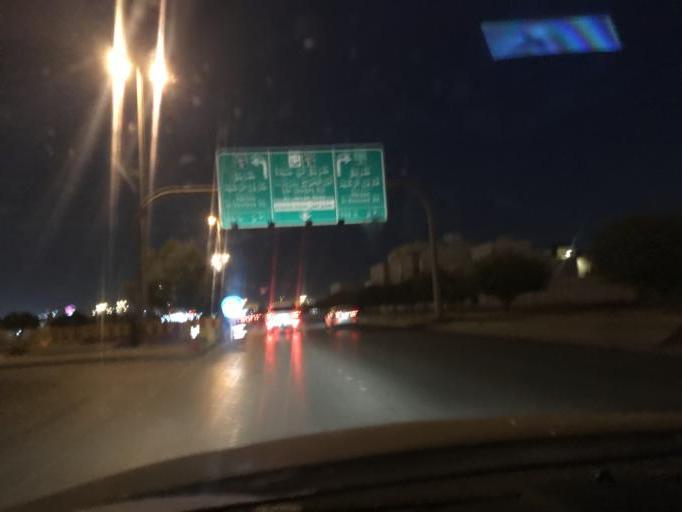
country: SA
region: Ar Riyad
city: Riyadh
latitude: 24.6673
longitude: 46.8029
